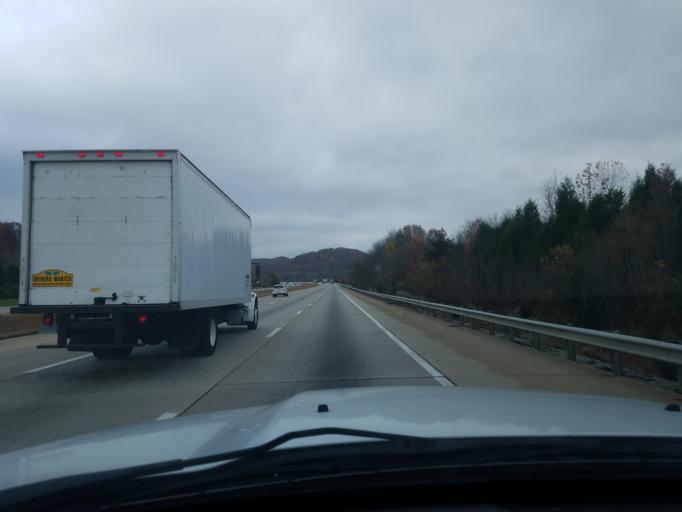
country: US
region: Kentucky
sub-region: Bullitt County
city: Lebanon Junction
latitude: 37.9024
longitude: -85.6955
